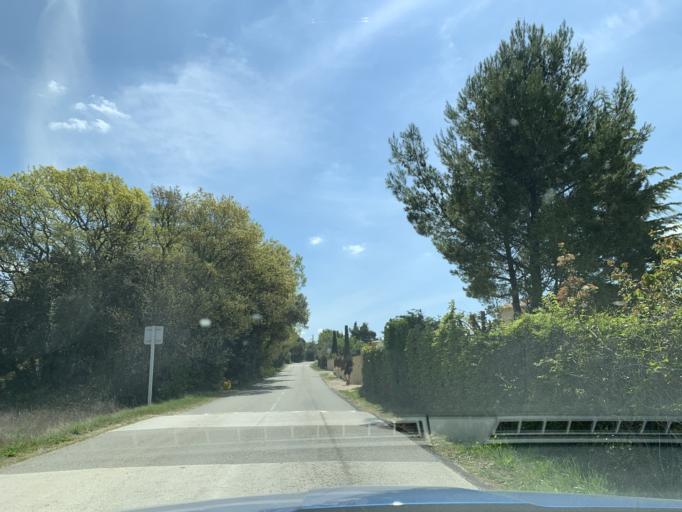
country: FR
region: Provence-Alpes-Cote d'Azur
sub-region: Departement du Vaucluse
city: Saint-Didier
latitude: 43.9853
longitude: 5.1100
